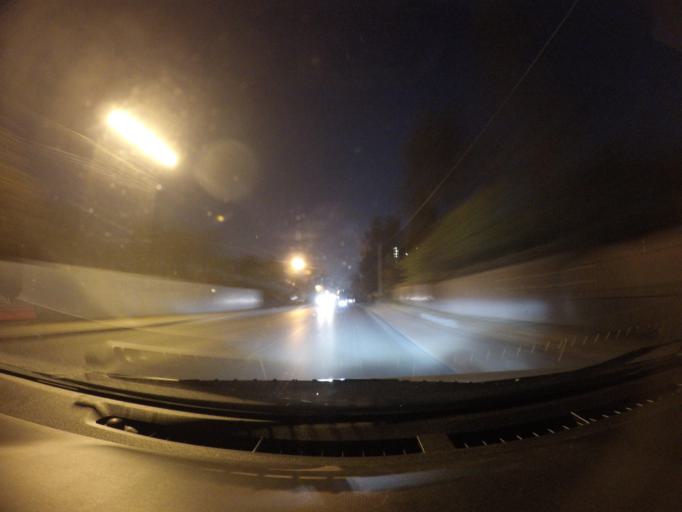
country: RU
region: Moskovskaya
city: Novopodrezkovo
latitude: 55.9237
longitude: 37.3711
